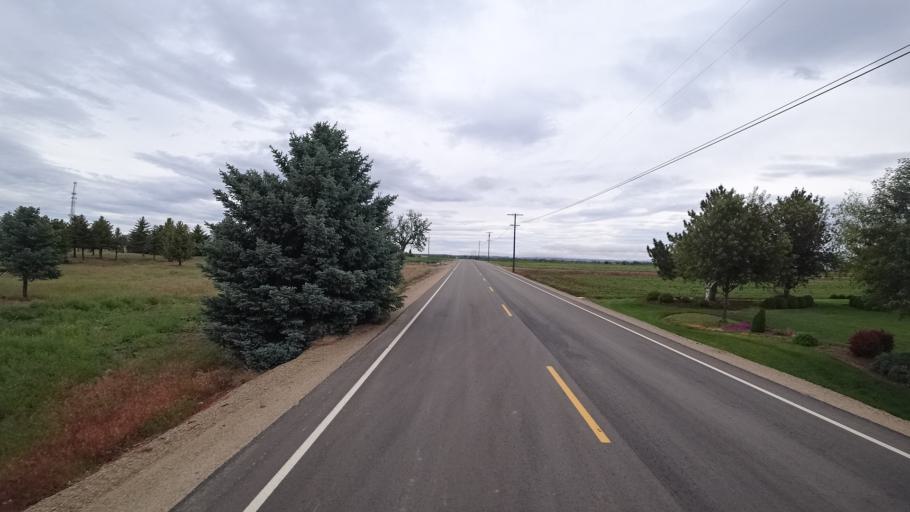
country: US
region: Idaho
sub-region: Ada County
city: Star
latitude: 43.6662
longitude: -116.5129
